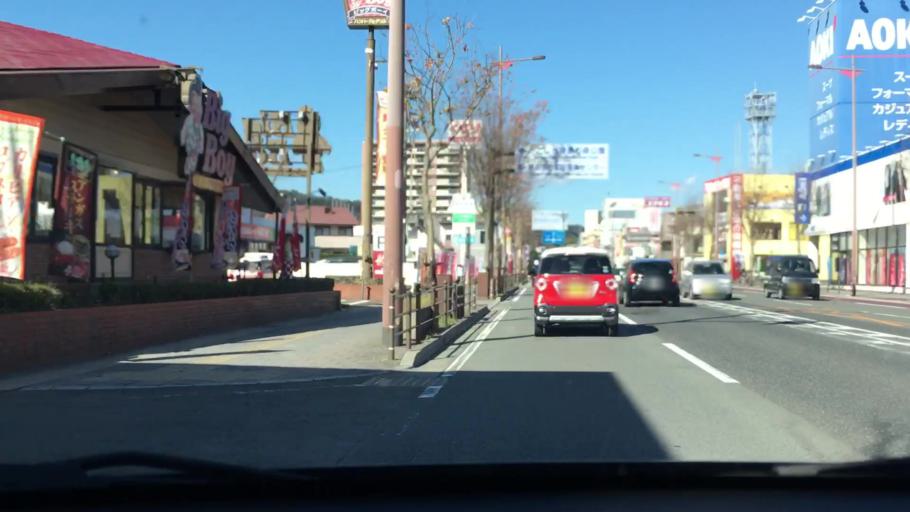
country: JP
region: Kagoshima
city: Kagoshima-shi
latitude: 31.6132
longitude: 130.5314
